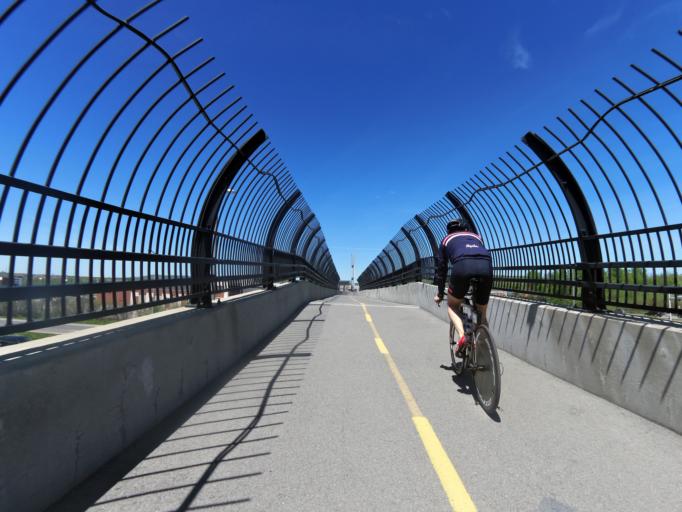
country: CA
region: Ontario
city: Ottawa
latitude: 45.4312
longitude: -75.7783
